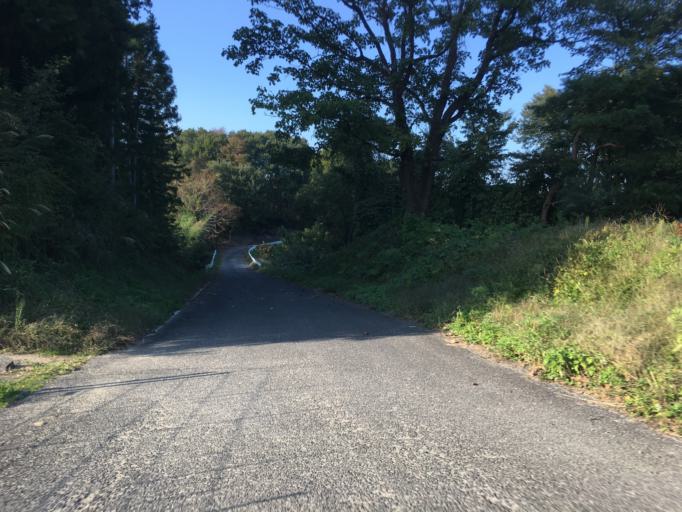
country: JP
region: Fukushima
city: Nihommatsu
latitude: 37.6384
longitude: 140.5626
